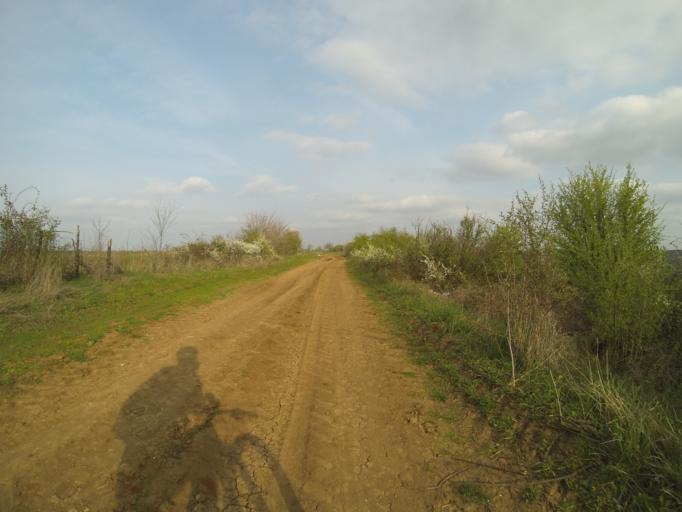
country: RO
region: Dolj
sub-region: Comuna Podari
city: Podari
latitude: 44.2477
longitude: 23.7572
